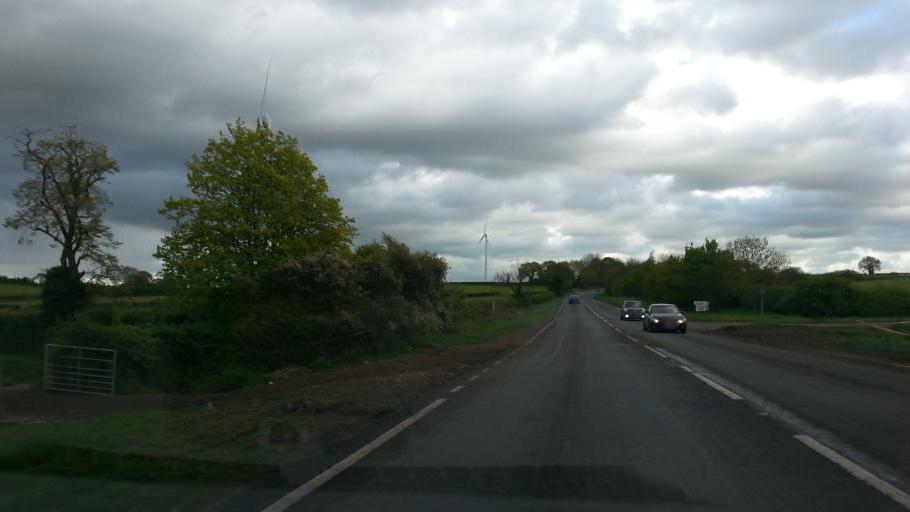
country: GB
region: England
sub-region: Nottinghamshire
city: Farndon
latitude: 53.1202
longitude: -0.8709
